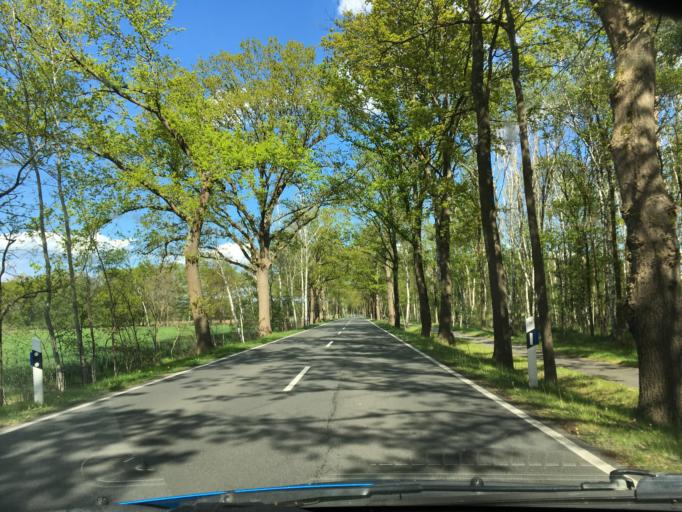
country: DE
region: Lower Saxony
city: Trebel
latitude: 52.9739
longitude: 11.2857
